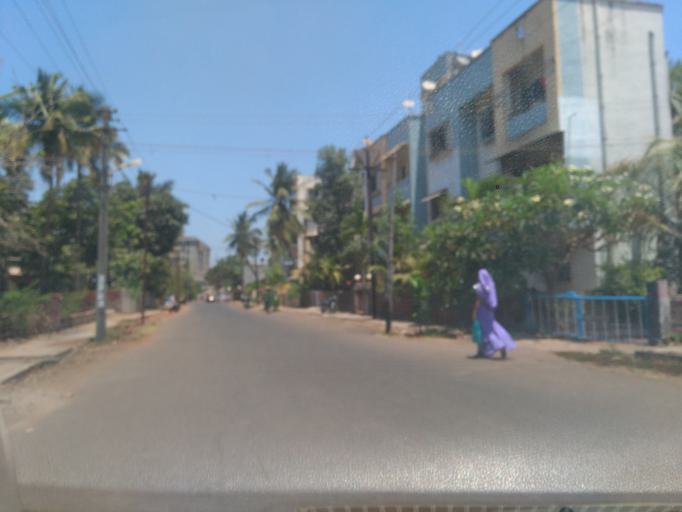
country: IN
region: Maharashtra
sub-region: Ratnagiri
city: Ratnagiri
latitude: 16.9843
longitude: 73.3149
